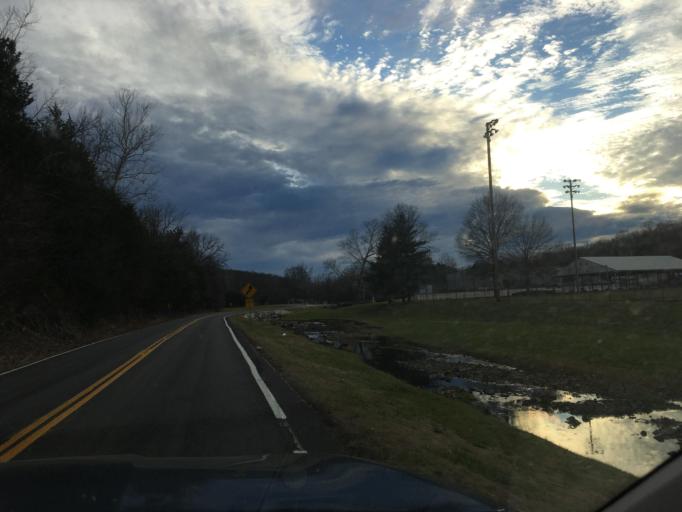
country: US
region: Missouri
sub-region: Jefferson County
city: De Soto
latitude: 38.1124
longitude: -90.5619
